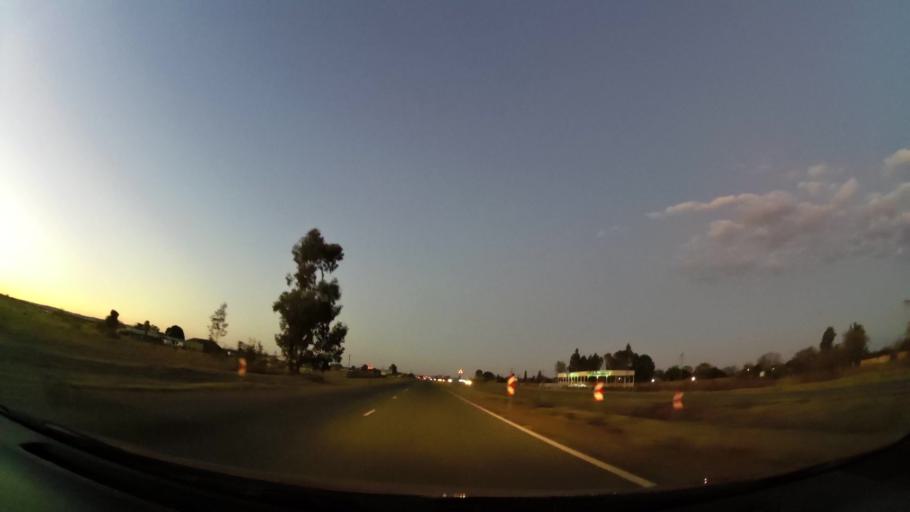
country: ZA
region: North-West
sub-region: Dr Kenneth Kaunda District Municipality
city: Potchefstroom
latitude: -26.7026
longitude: 27.1270
